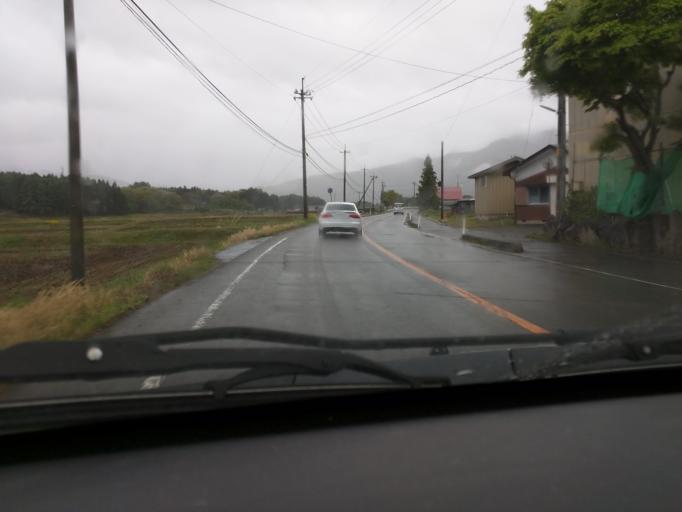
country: JP
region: Fukushima
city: Inawashiro
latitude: 37.5718
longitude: 140.1164
